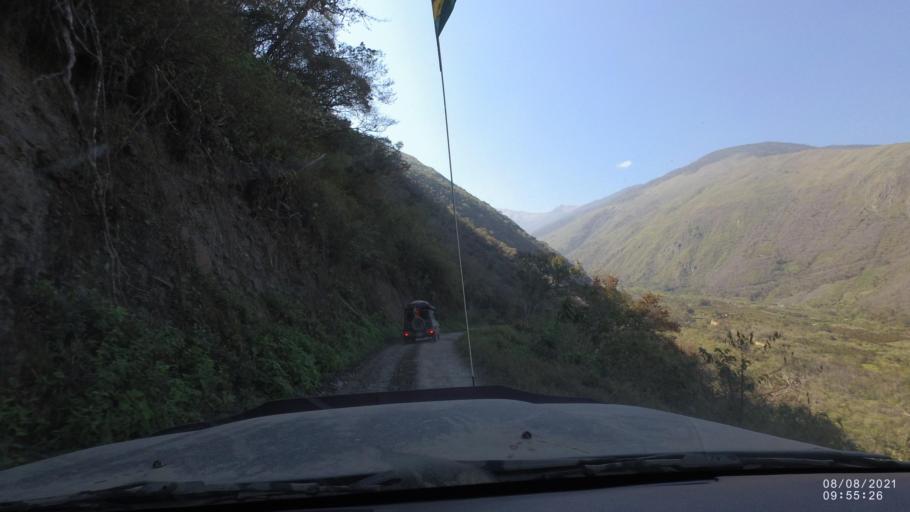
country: BO
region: La Paz
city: Quime
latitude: -16.6346
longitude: -66.7295
